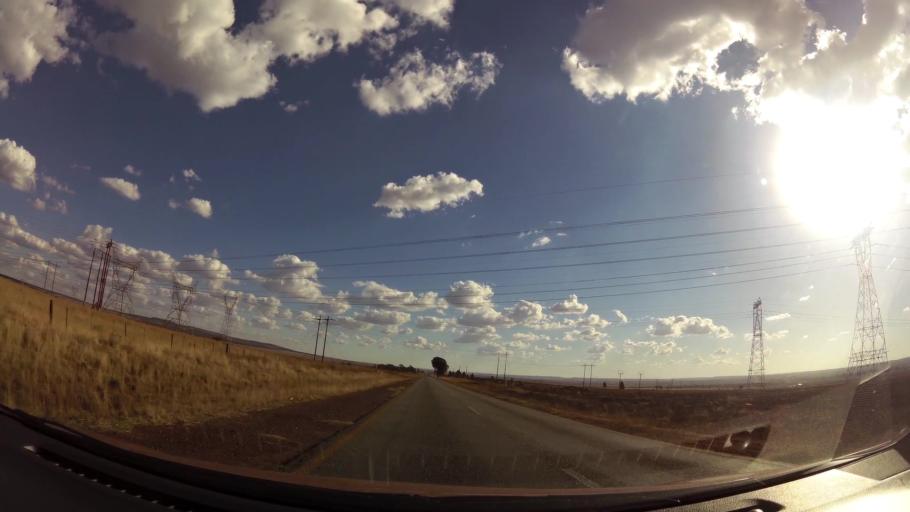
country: ZA
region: Gauteng
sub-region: West Rand District Municipality
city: Carletonville
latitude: -26.3973
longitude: 27.3045
